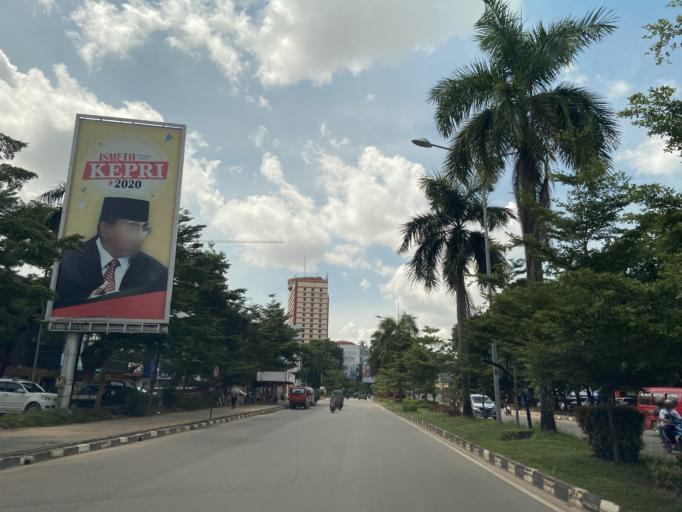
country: SG
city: Singapore
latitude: 1.1523
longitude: 104.0044
